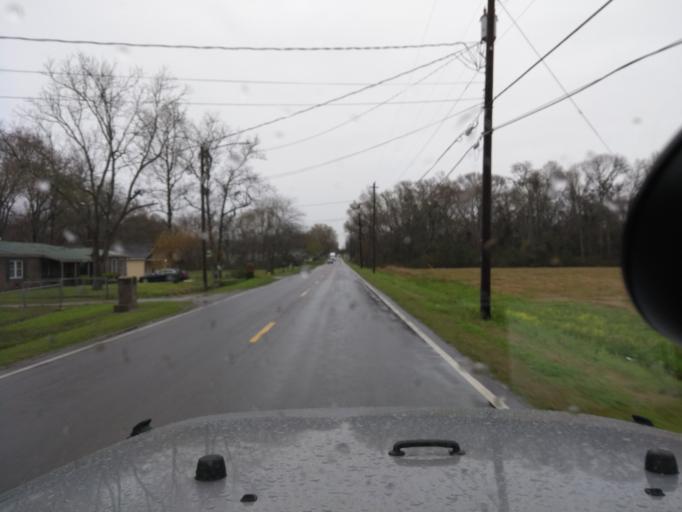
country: US
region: Georgia
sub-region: Chatham County
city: Garden City
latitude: 32.0907
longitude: -81.1446
